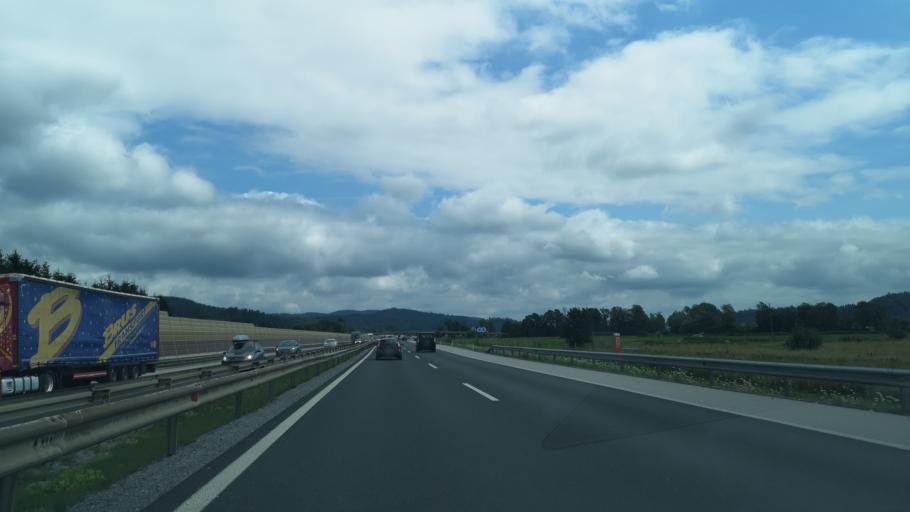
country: SI
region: Vrhnika
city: Verd
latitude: 45.9909
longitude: 14.3266
